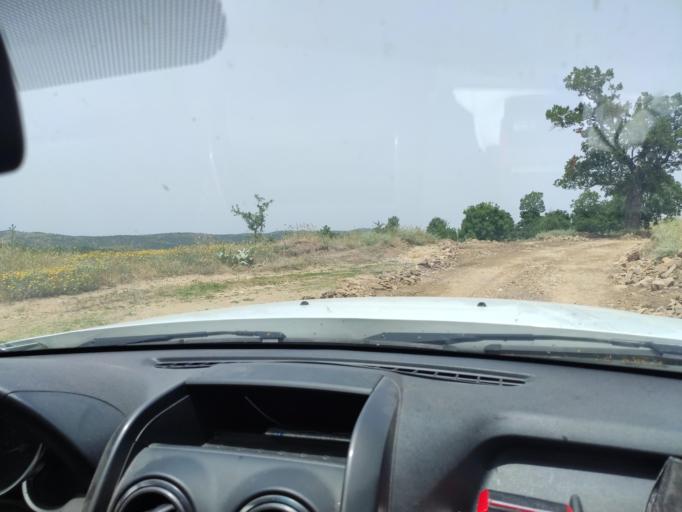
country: MK
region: Radovis
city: Radovish
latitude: 41.6765
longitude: 22.4007
